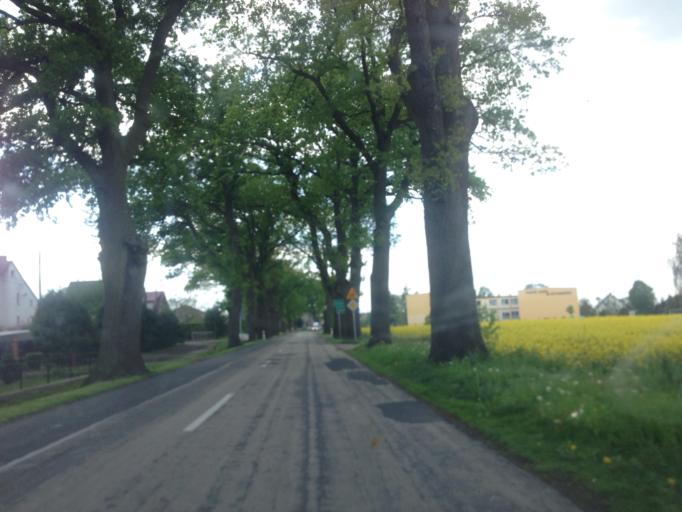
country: PL
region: Kujawsko-Pomorskie
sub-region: Powiat swiecki
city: Pruszcz
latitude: 53.2852
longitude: 18.1295
